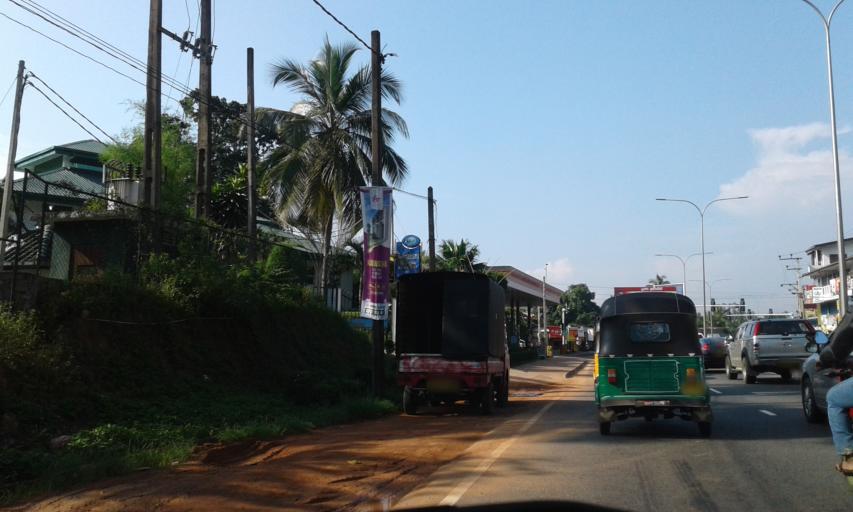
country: LK
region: Western
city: Gampaha
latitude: 7.0358
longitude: 79.9912
